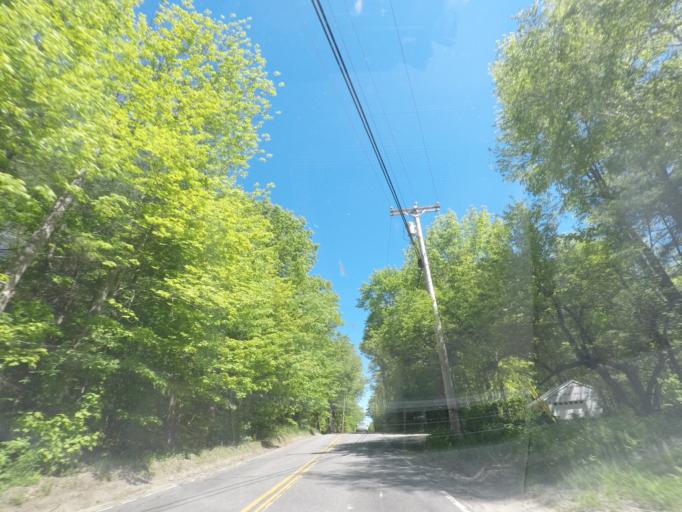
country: US
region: Maine
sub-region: Kennebec County
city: Manchester
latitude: 44.2846
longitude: -69.8894
